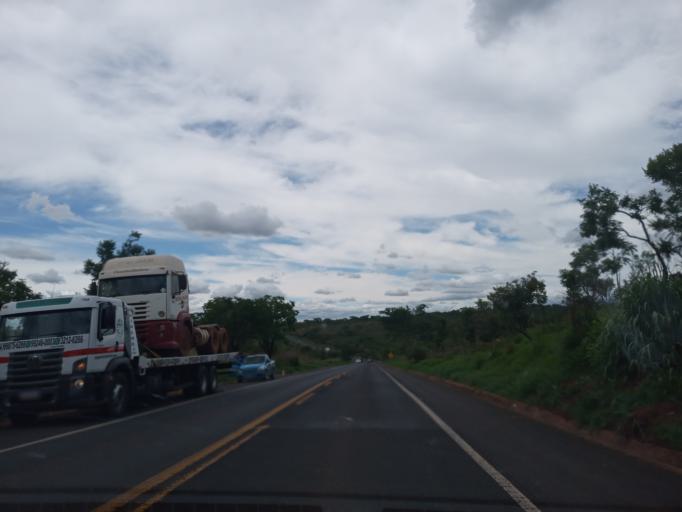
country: BR
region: Minas Gerais
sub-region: Uberlandia
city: Uberlandia
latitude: -19.1724
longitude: -47.8927
